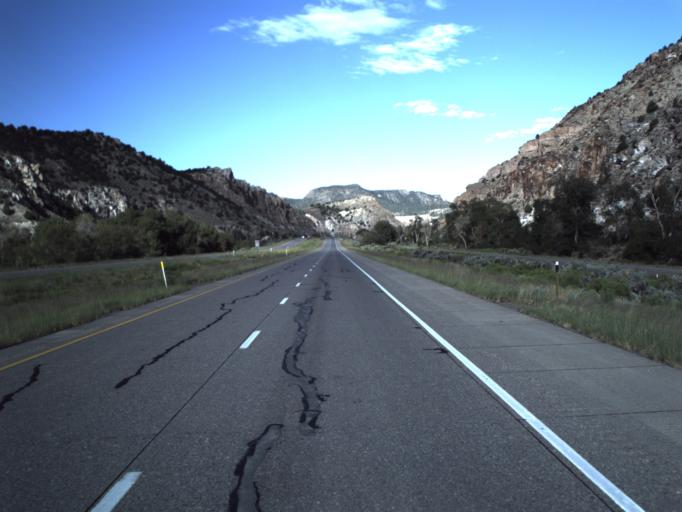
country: US
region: Utah
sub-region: Sevier County
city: Monroe
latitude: 38.5799
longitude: -112.3057
